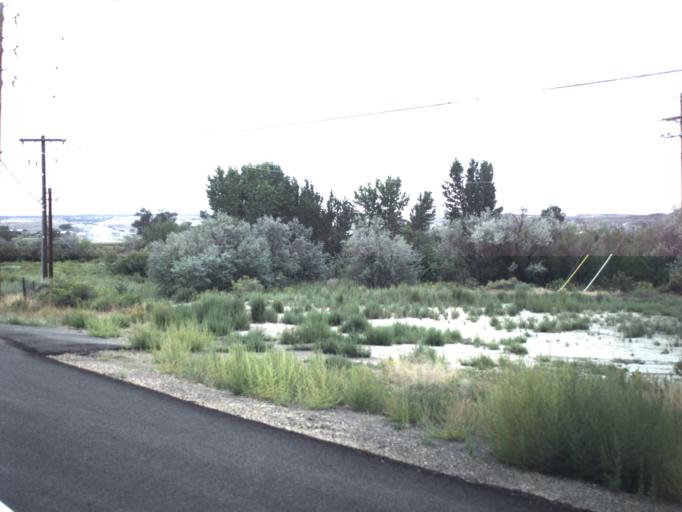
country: US
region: Utah
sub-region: Carbon County
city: Wellington
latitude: 39.5425
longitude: -110.7026
